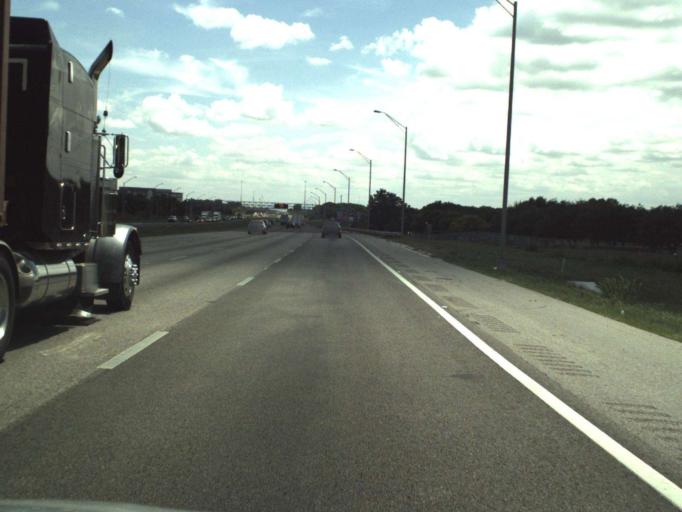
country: US
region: Florida
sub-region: Seminole County
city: Heathrow
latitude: 28.7721
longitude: -81.3579
